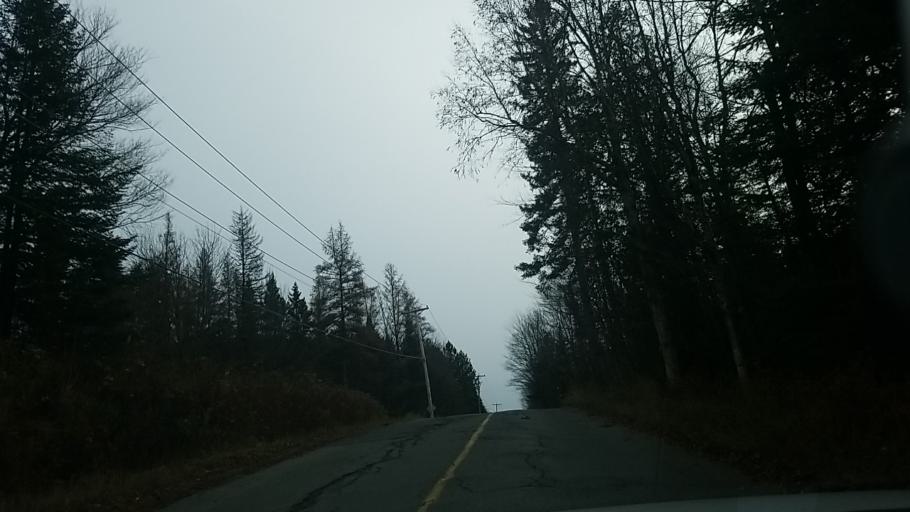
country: CA
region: Quebec
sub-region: Laurentides
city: Saint-Sauveur
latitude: 45.8228
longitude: -74.2481
